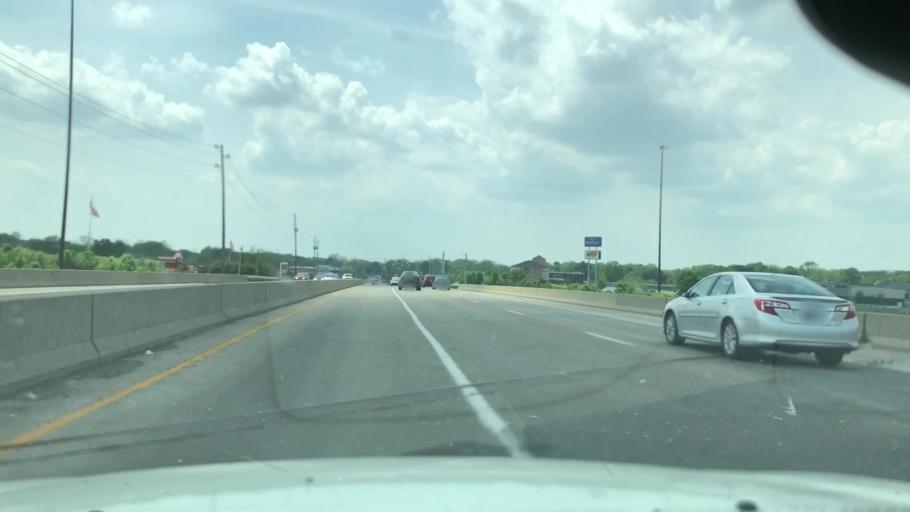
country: US
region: Indiana
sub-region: Marion County
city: Southport
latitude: 39.6658
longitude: -86.0892
